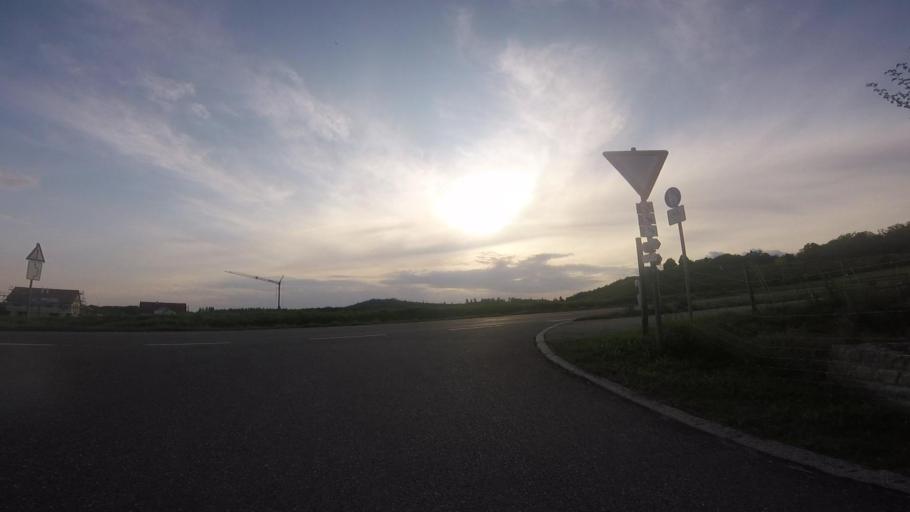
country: DE
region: Baden-Wuerttemberg
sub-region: Regierungsbezirk Stuttgart
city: Oberstenfeld
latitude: 48.9958
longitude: 9.3552
